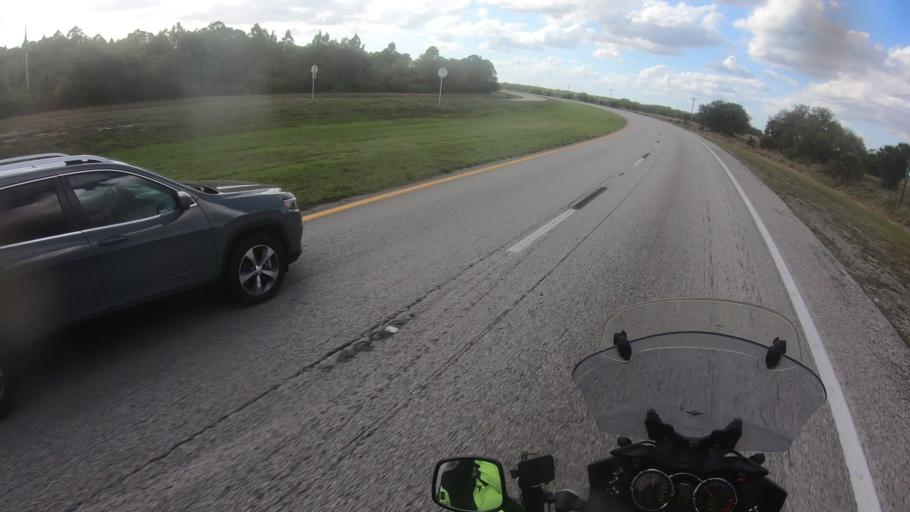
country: US
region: Florida
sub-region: Glades County
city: Moore Haven
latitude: 26.9001
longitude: -81.2397
